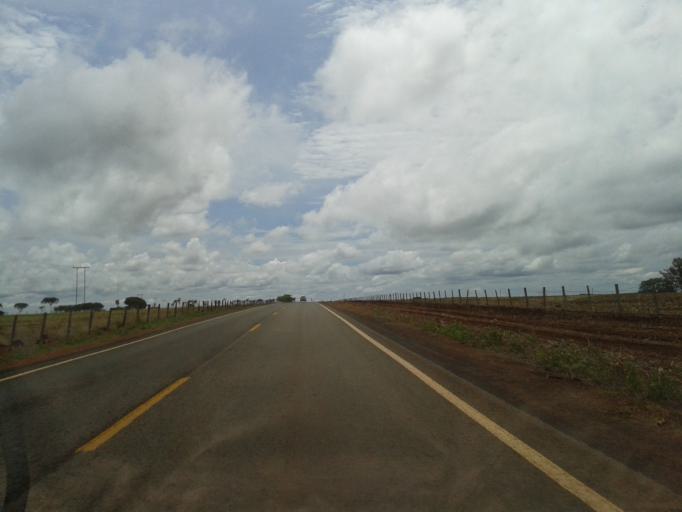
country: BR
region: Goias
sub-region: Buriti Alegre
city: Buriti Alegre
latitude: -18.1393
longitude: -49.0051
